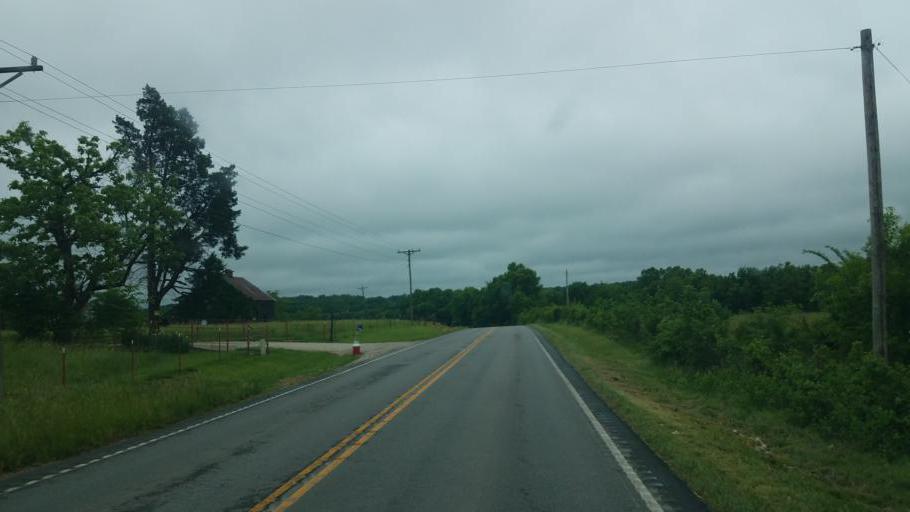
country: US
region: Missouri
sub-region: Moniteau County
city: California
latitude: 38.5937
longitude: -92.5738
